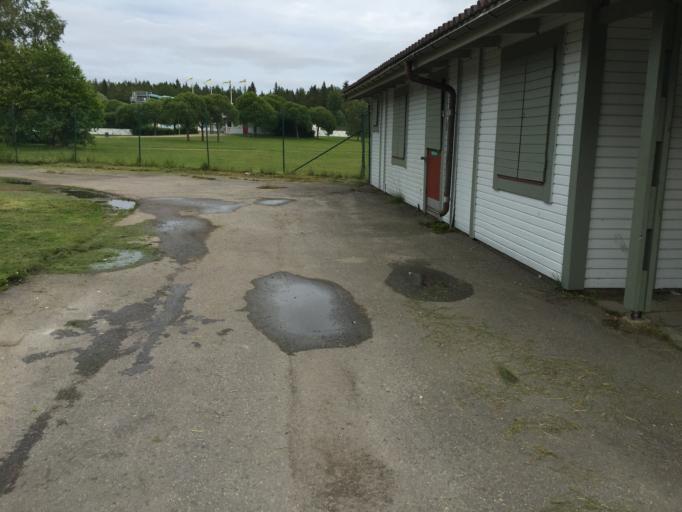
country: SE
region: Vaesterbotten
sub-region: Umea Kommun
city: Ersmark
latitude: 63.8370
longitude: 20.3388
